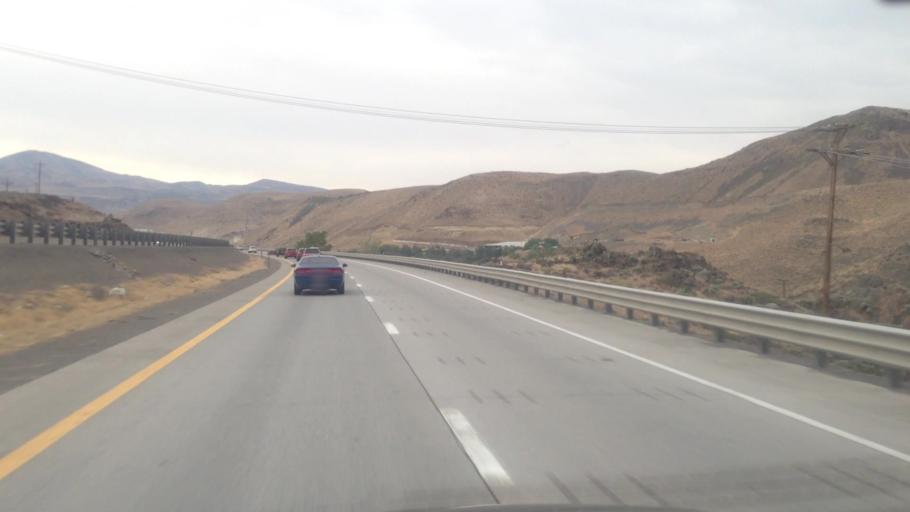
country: US
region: Nevada
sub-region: Washoe County
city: Sparks
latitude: 39.5111
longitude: -119.6668
